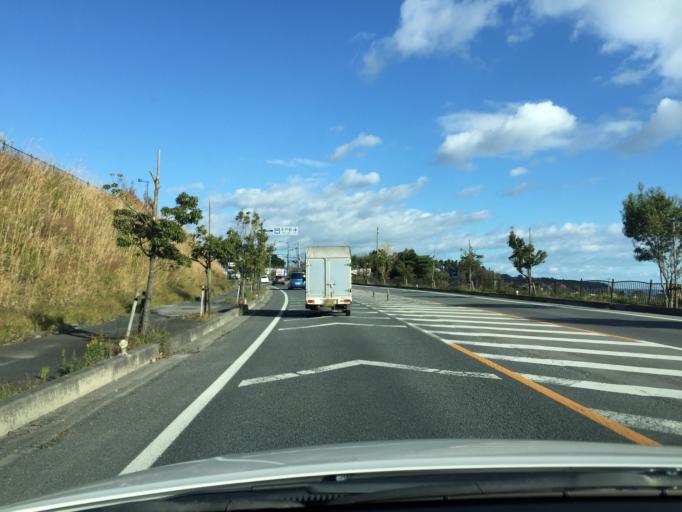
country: JP
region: Fukushima
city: Iwaki
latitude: 37.2502
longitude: 140.9980
